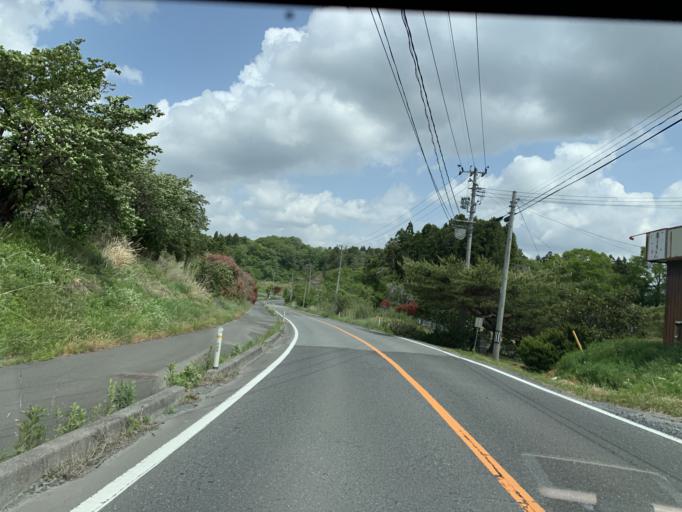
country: JP
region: Miyagi
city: Kogota
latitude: 38.6590
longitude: 141.0617
